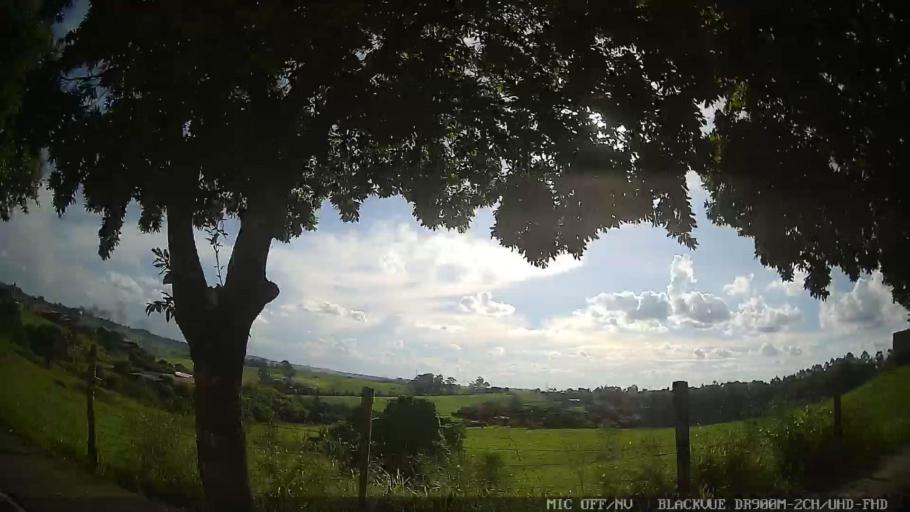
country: BR
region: Sao Paulo
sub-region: Tiete
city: Tiete
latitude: -23.0899
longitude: -47.7803
